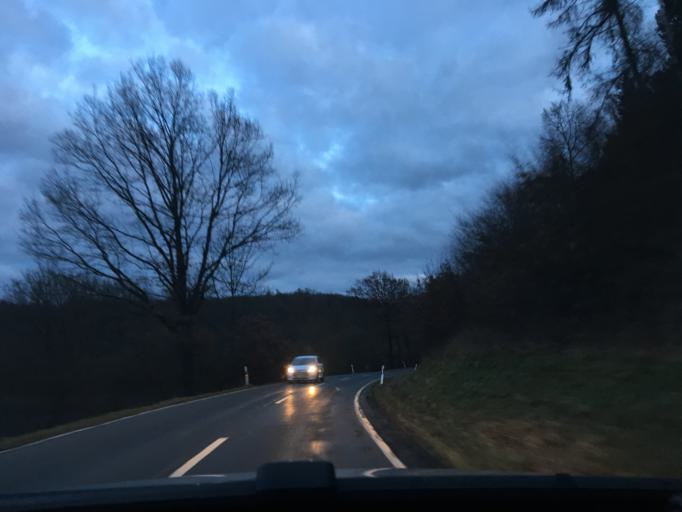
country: DE
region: Rheinland-Pfalz
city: Oberwiesen
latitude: 49.6898
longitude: 7.9637
